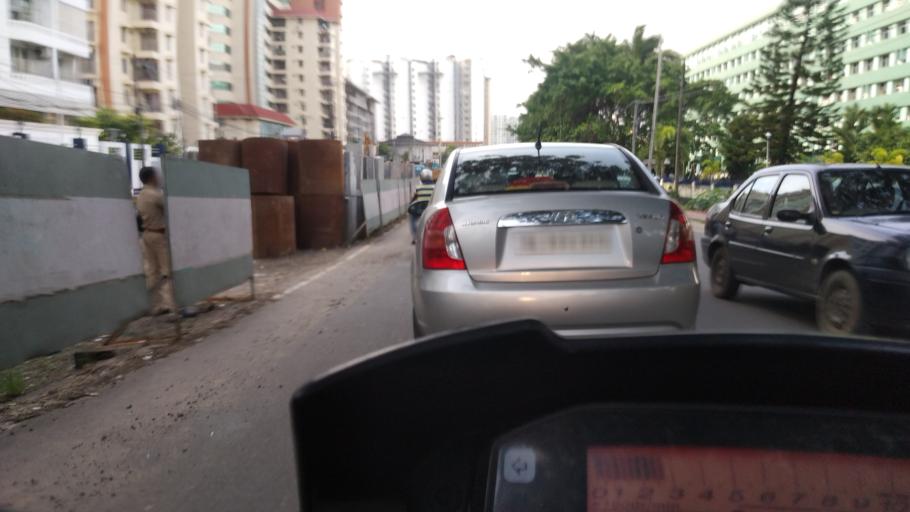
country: IN
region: Kerala
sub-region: Ernakulam
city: Cochin
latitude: 9.9869
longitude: 76.2722
